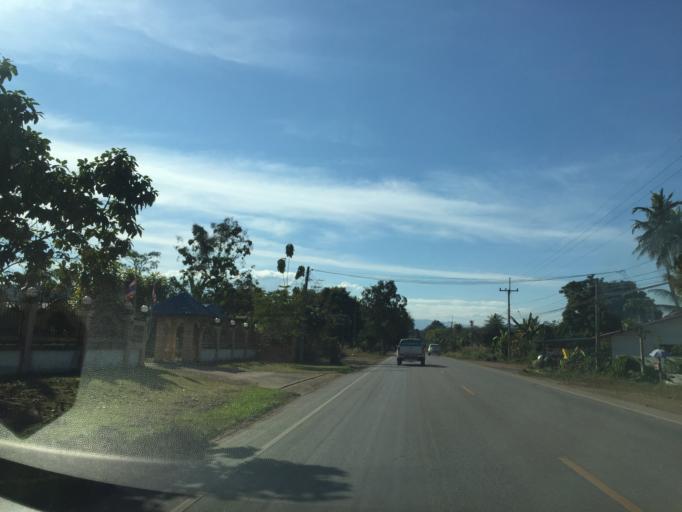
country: TH
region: Loei
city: Wang Saphung
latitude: 17.3153
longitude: 101.7480
